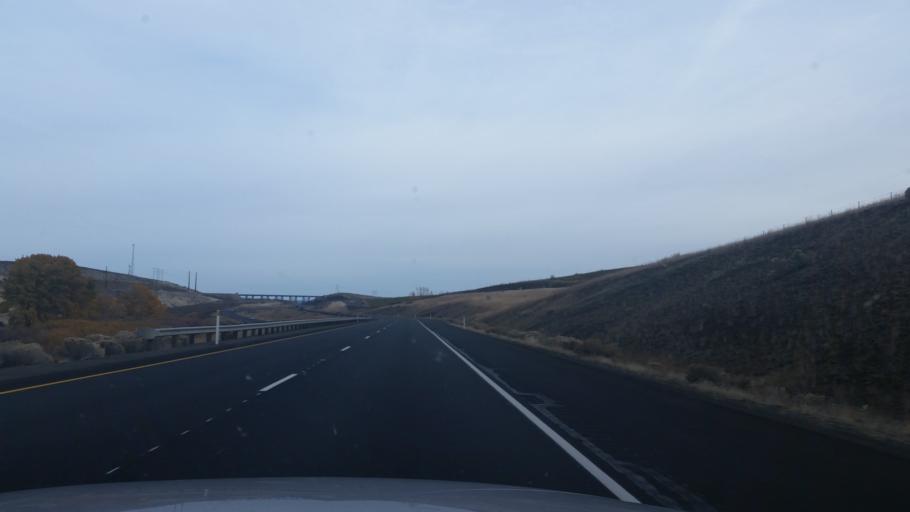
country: US
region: Washington
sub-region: Kittitas County
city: Kittitas
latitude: 46.9593
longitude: -120.3223
